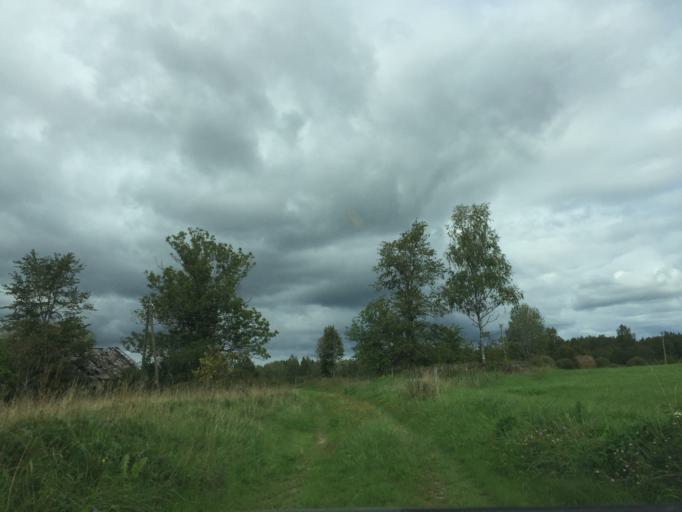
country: LV
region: Pargaujas
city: Stalbe
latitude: 57.4959
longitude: 24.9135
